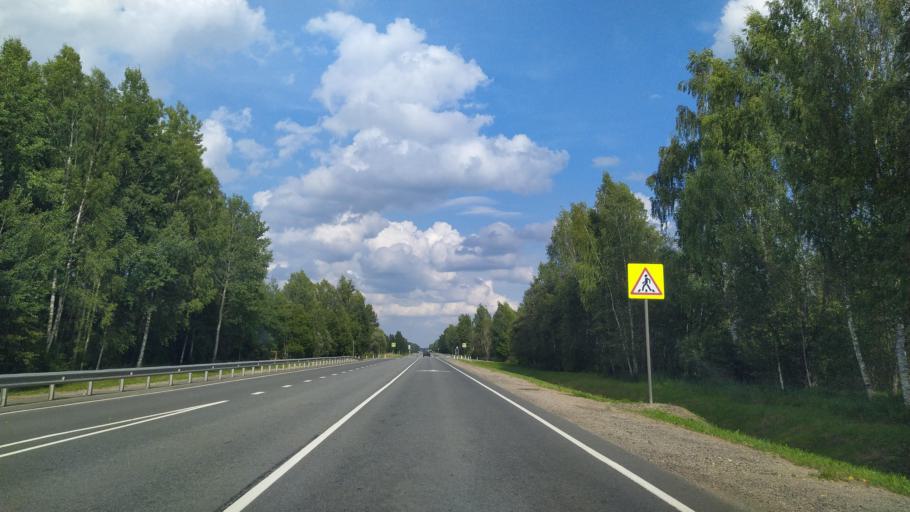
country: RU
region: Novgorod
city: Sol'tsy
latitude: 58.1661
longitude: 30.4688
